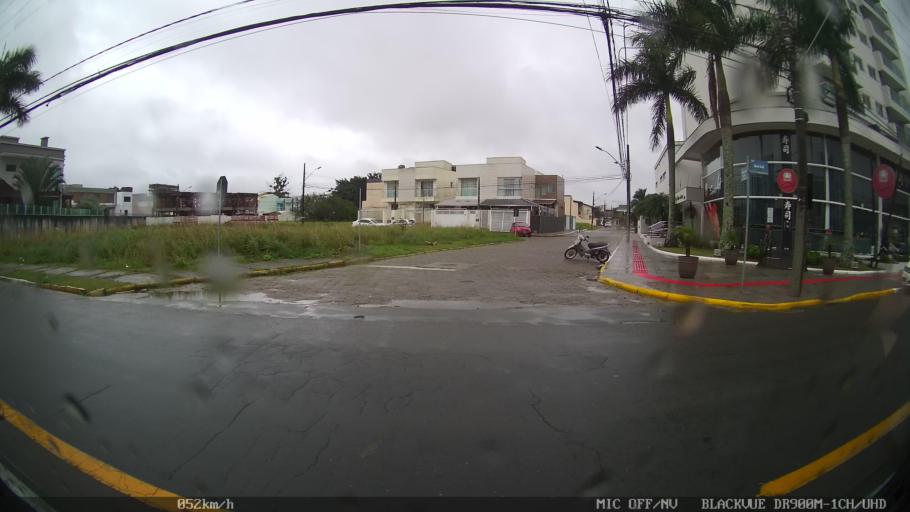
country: BR
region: Santa Catarina
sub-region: Itajai
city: Itajai
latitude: -26.9228
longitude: -48.6802
